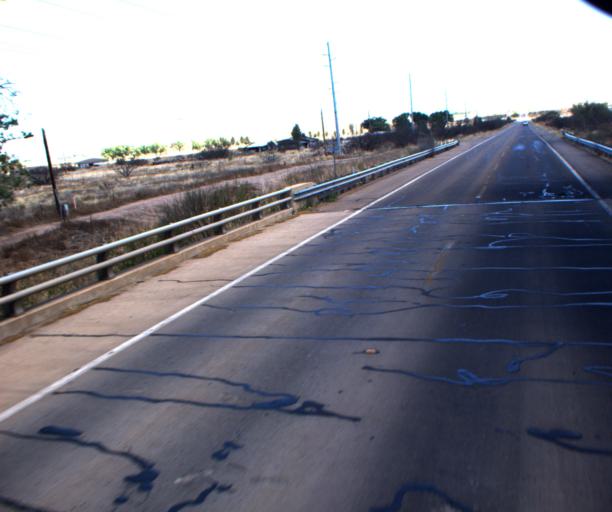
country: US
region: Arizona
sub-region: Cochise County
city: Sierra Vista Southeast
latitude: 31.3800
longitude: -110.1107
